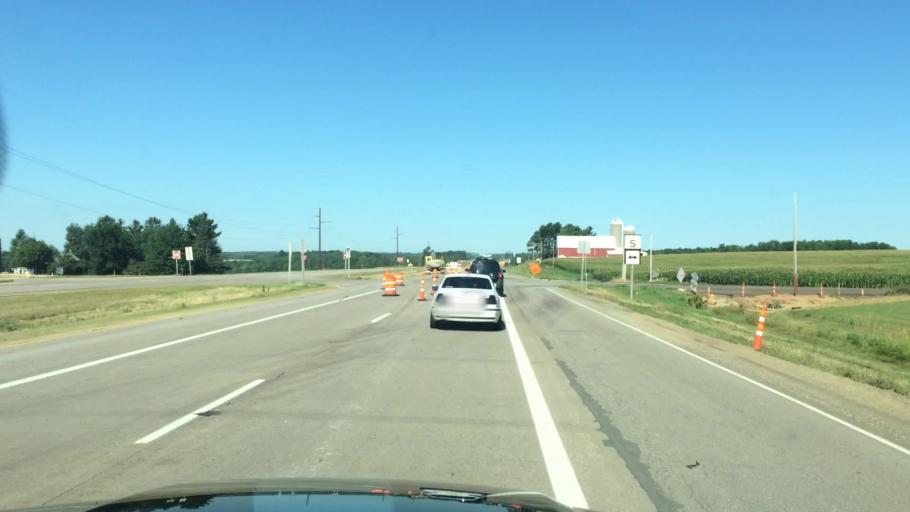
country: US
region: Wisconsin
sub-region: Marathon County
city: Edgar
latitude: 44.9446
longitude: -89.9044
